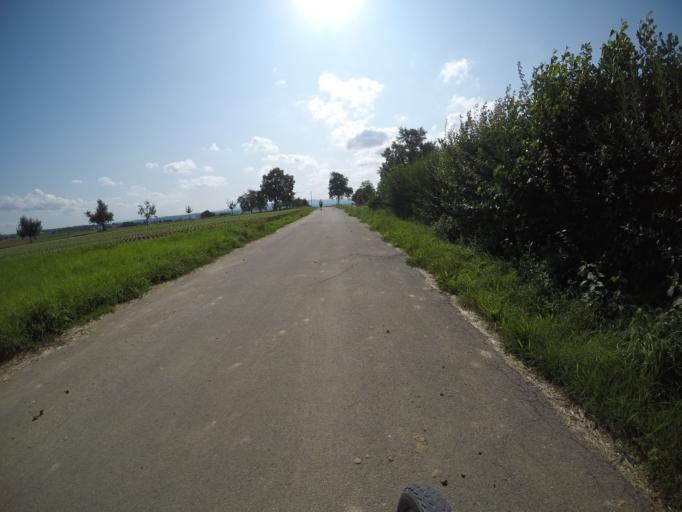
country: DE
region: Baden-Wuerttemberg
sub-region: Regierungsbezirk Stuttgart
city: Kongen
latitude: 48.6879
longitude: 9.3430
